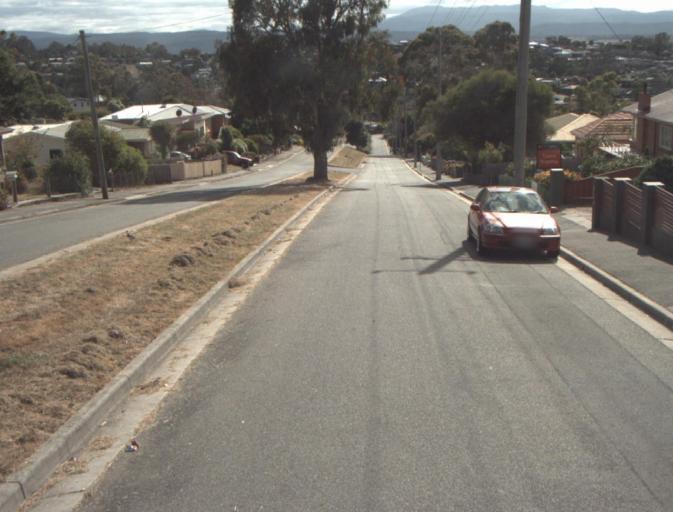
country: AU
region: Tasmania
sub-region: Launceston
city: Summerhill
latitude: -41.4652
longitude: 147.1178
